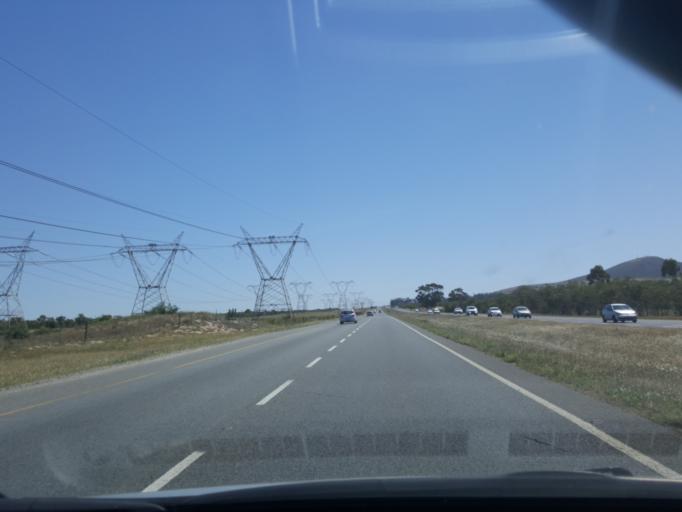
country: ZA
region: Western Cape
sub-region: City of Cape Town
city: Sunset Beach
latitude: -33.7489
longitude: 18.5463
